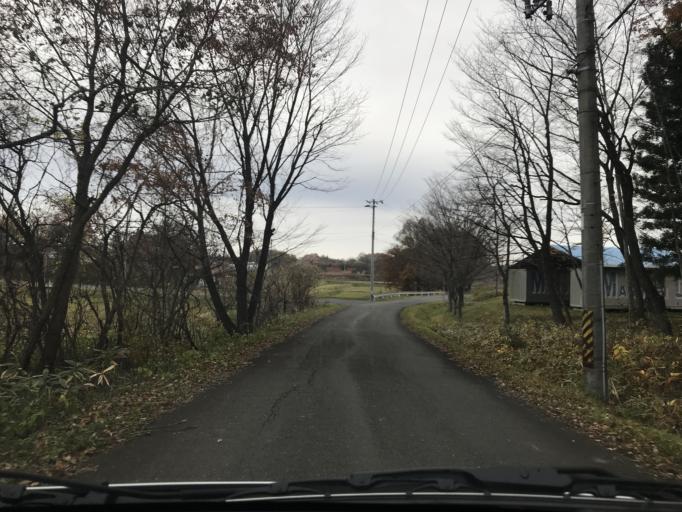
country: JP
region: Iwate
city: Ichinoseki
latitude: 38.9916
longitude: 141.0148
